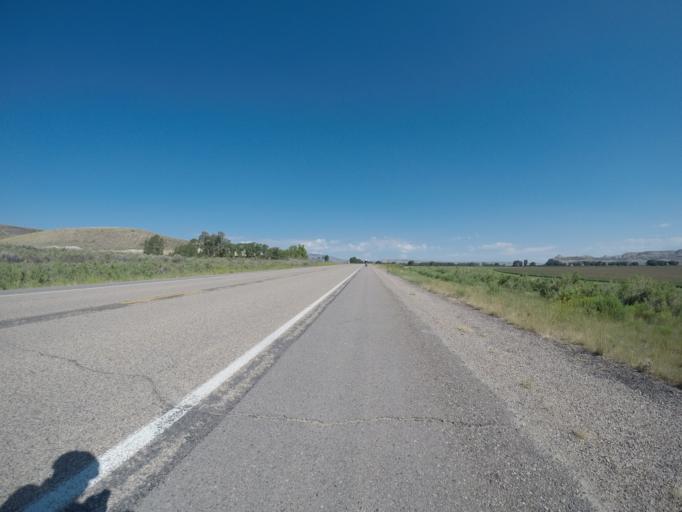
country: US
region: Wyoming
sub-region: Sublette County
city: Marbleton
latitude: 42.2082
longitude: -110.1843
